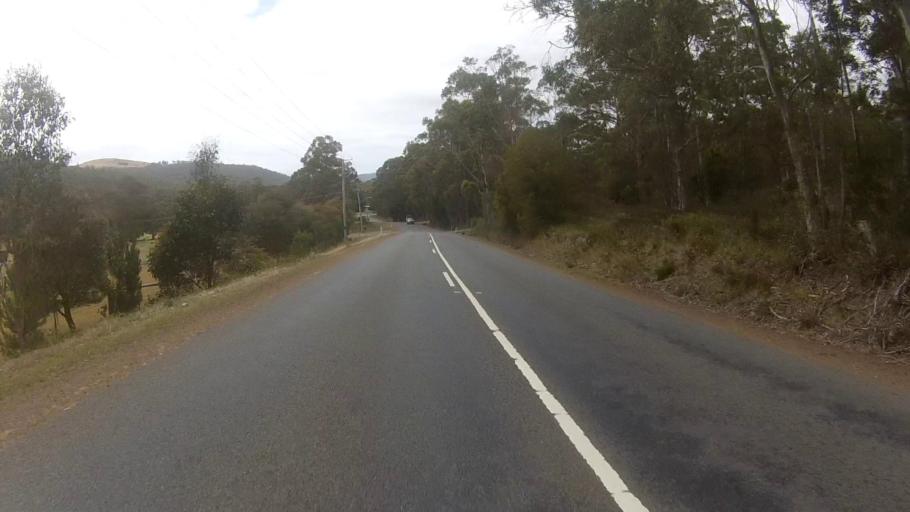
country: AU
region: Tasmania
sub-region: Kingborough
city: Margate
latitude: -42.9927
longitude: 147.2166
